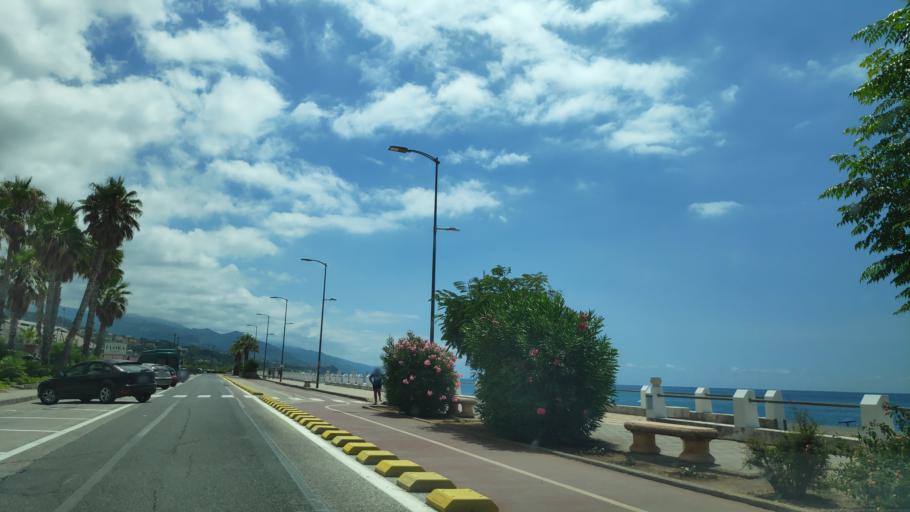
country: IT
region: Calabria
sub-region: Provincia di Cosenza
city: Paola
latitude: 39.3559
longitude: 16.0331
